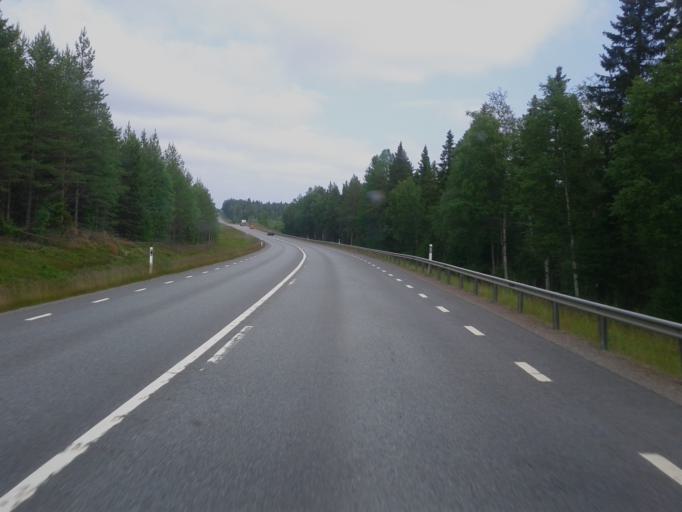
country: SE
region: Vaesterbotten
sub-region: Skelleftea Kommun
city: Burea
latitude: 64.3496
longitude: 21.2923
